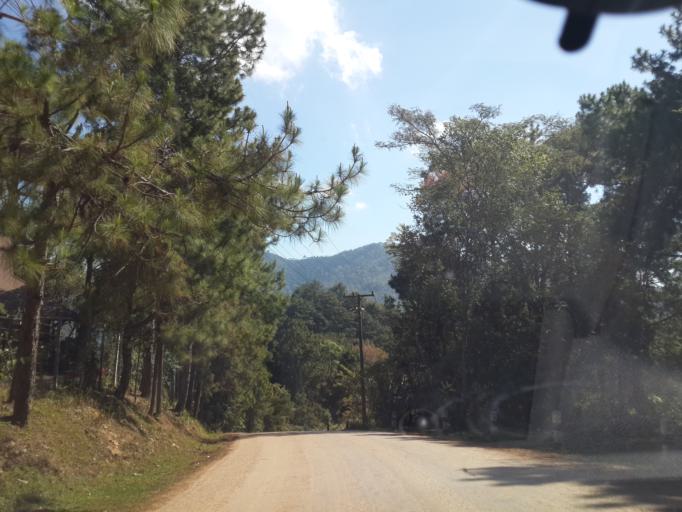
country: TH
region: Chiang Mai
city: Fang
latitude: 19.9258
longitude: 99.0454
